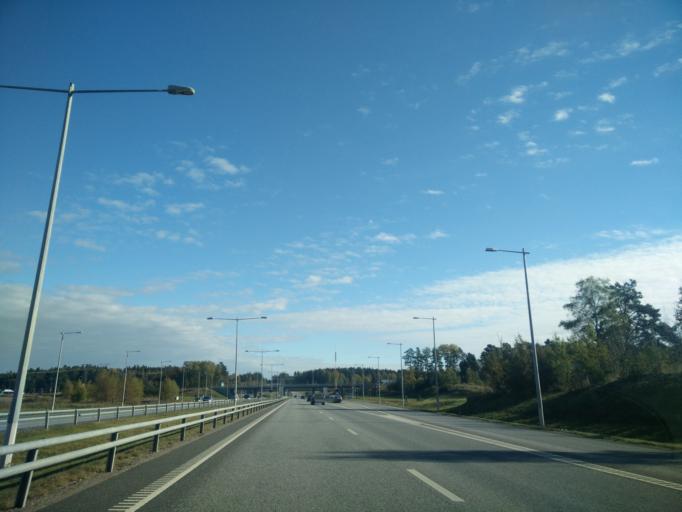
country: SE
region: Stockholm
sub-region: Taby Kommun
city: Taby
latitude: 59.4753
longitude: 18.0465
